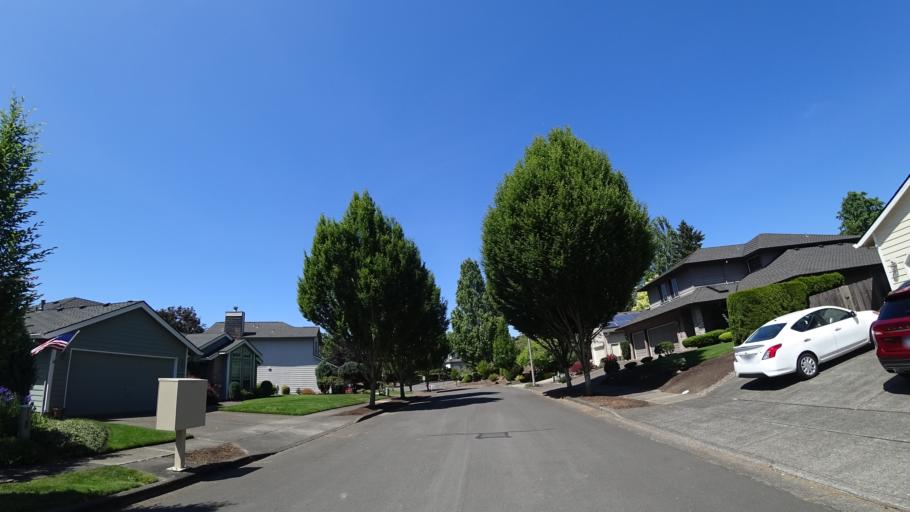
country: US
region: Oregon
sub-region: Washington County
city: King City
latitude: 45.4428
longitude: -122.8136
